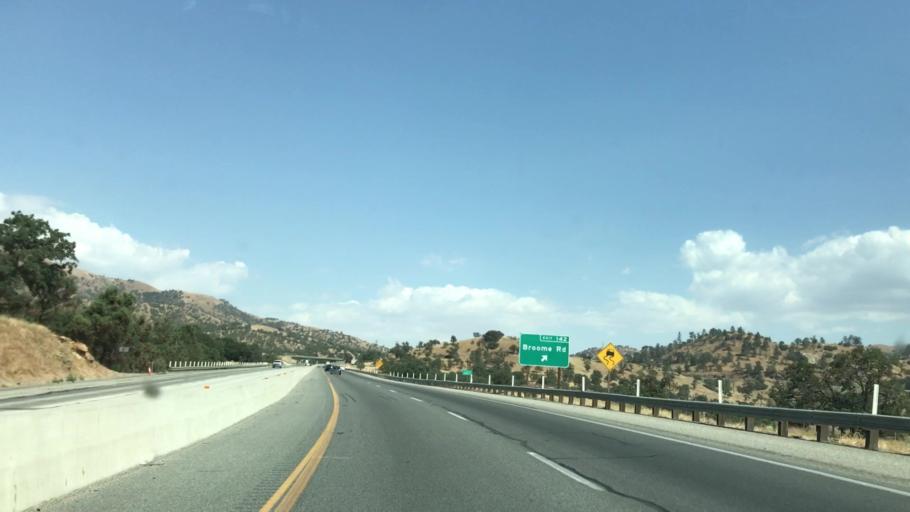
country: US
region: California
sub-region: Kern County
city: Golden Hills
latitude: 35.2035
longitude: -118.5299
